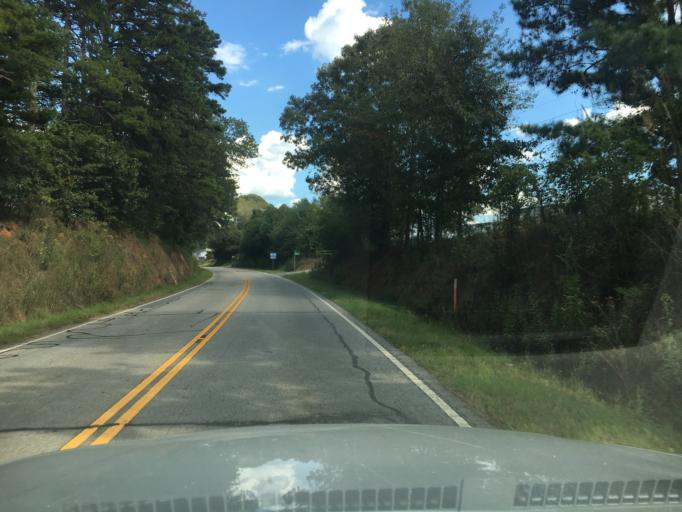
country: US
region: South Carolina
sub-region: Oconee County
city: Utica
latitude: 34.7121
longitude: -82.9012
